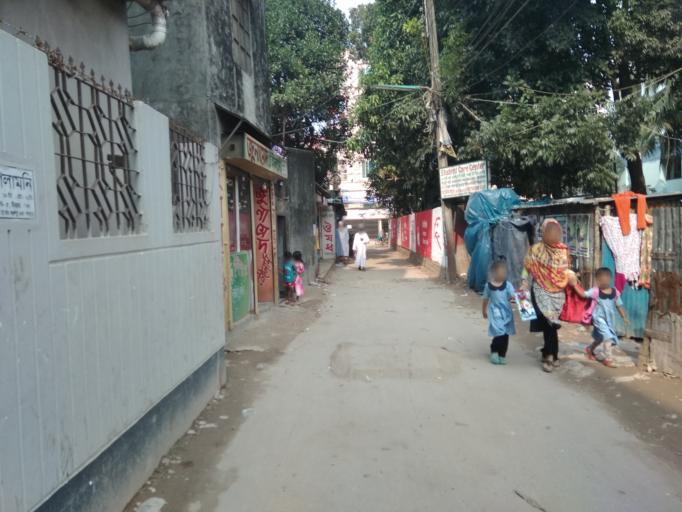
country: BD
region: Dhaka
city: Tungi
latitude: 23.8626
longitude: 90.3882
